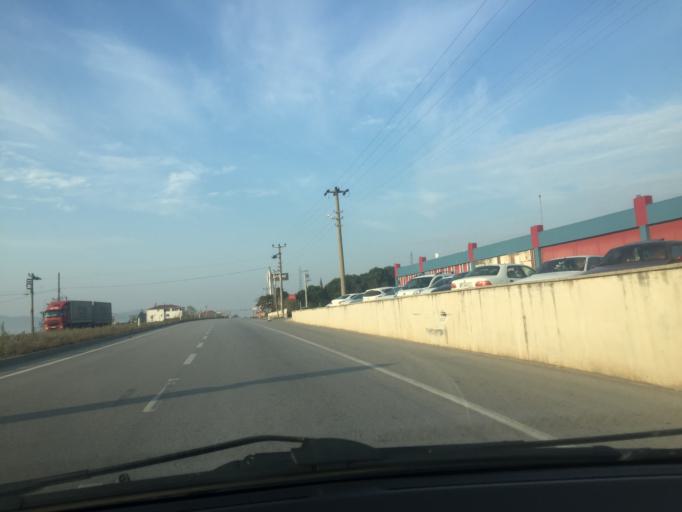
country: TR
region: Canakkale
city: Dimetoka
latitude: 40.2476
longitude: 27.2897
